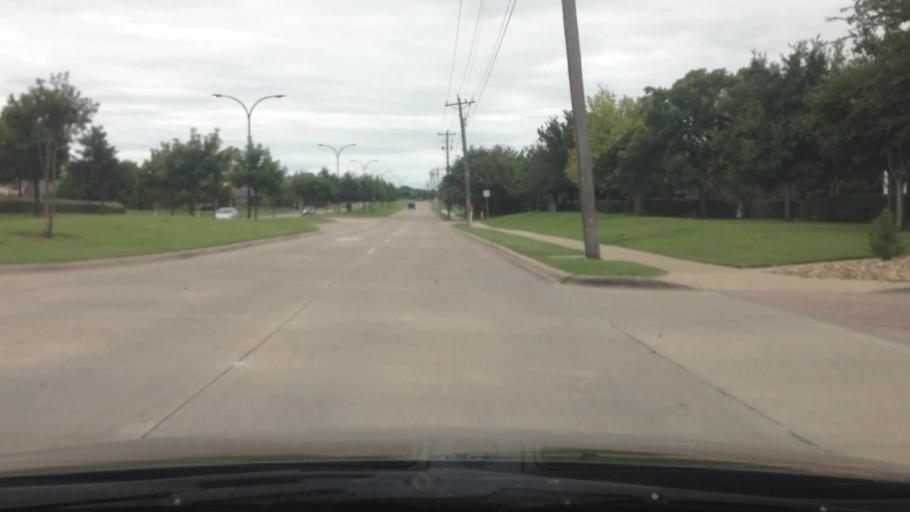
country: US
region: Texas
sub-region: Tarrant County
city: Keller
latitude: 32.8976
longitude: -97.2387
